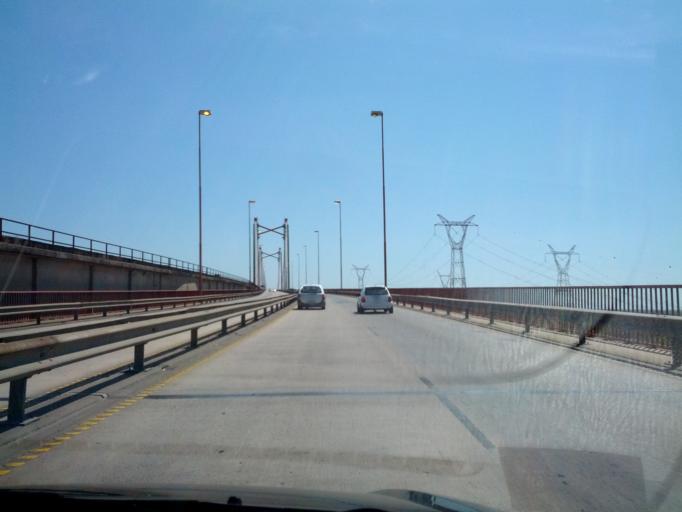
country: AR
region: Buenos Aires
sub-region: Partido de Zarate
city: Zarate
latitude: -34.1096
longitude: -59.0050
